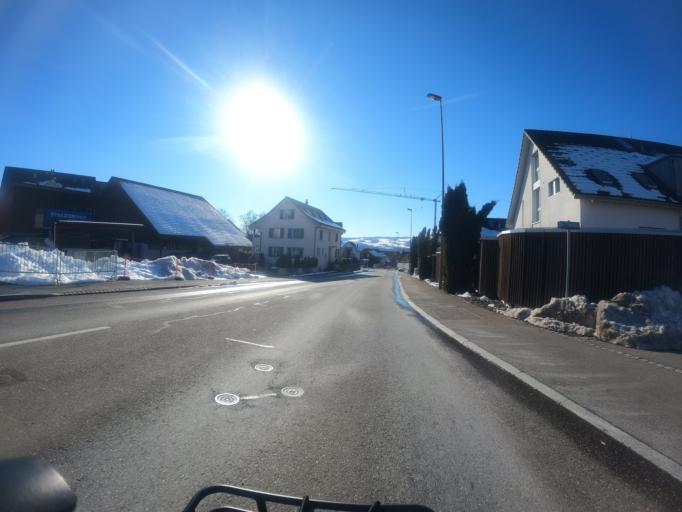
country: CH
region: Zurich
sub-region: Bezirk Affoltern
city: Ottenbach
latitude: 47.2831
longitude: 8.4072
